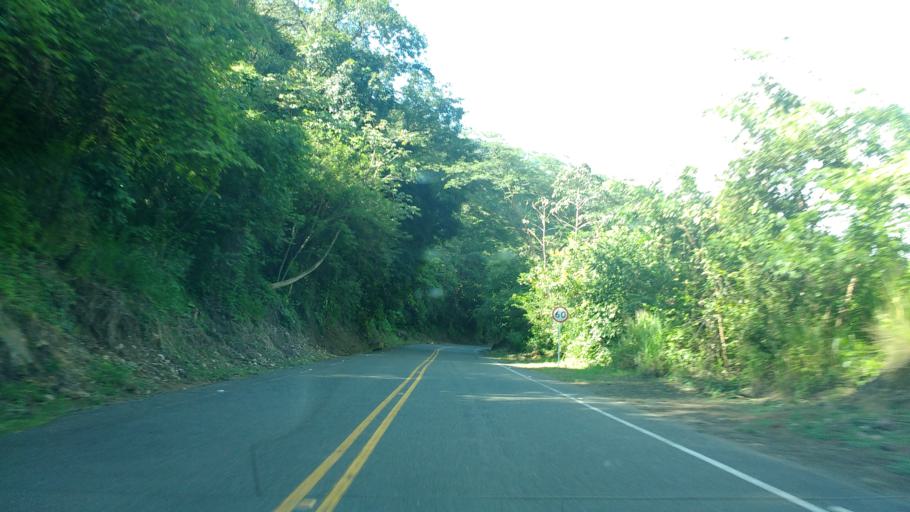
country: CO
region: Antioquia
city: Concordia
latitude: 6.0700
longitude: -75.8610
